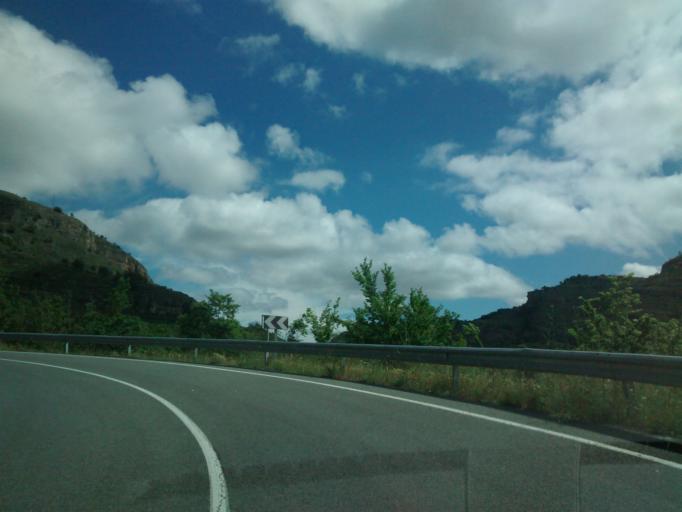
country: ES
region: La Rioja
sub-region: Provincia de La Rioja
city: Soto en Cameros
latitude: 42.2899
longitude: -2.4251
